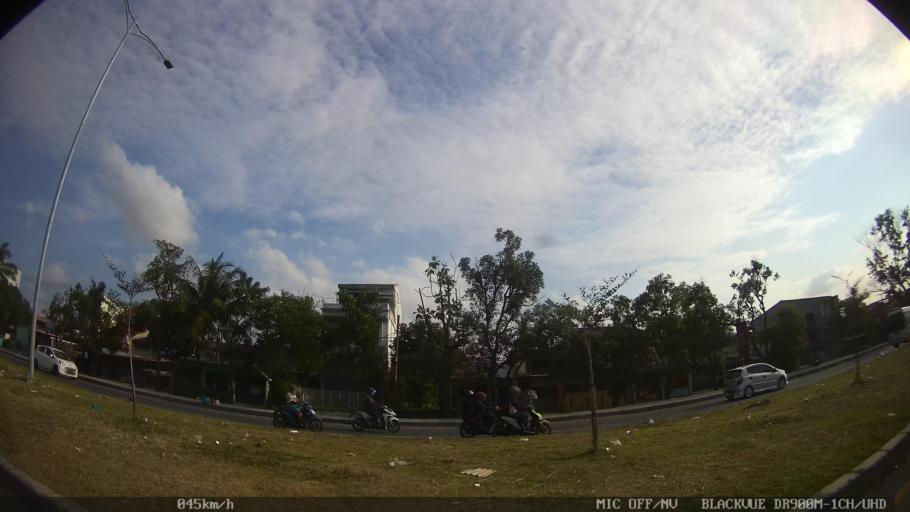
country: ID
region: North Sumatra
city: Medan
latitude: 3.6156
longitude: 98.6415
